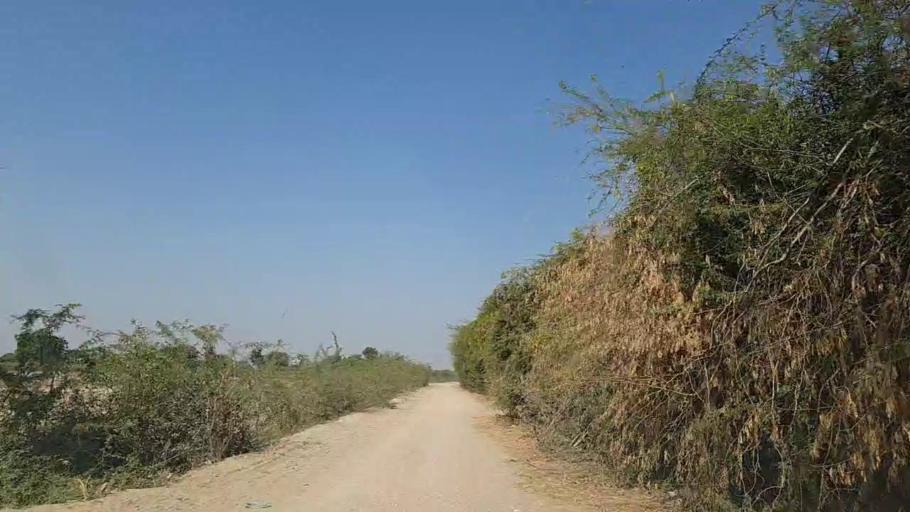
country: PK
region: Sindh
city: Naukot
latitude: 24.8646
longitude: 69.4036
